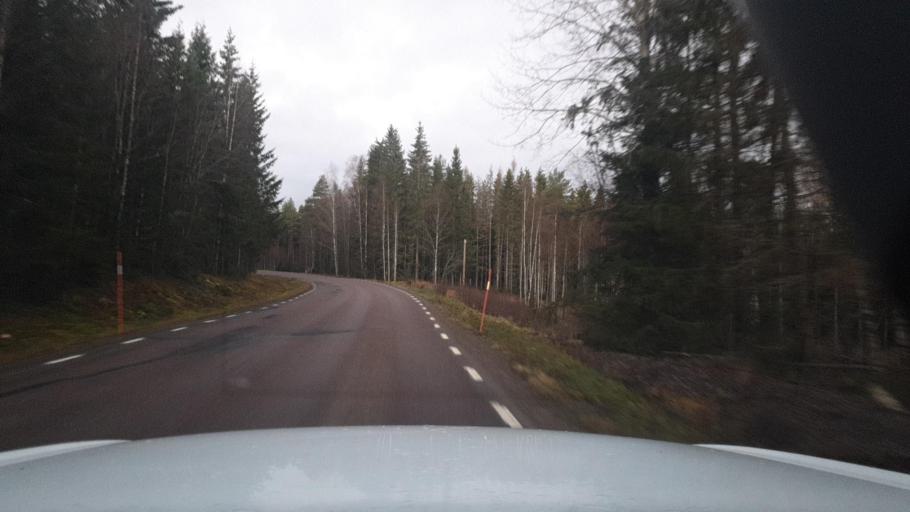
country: SE
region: Vaermland
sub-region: Eda Kommun
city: Amotfors
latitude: 59.8662
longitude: 12.4883
